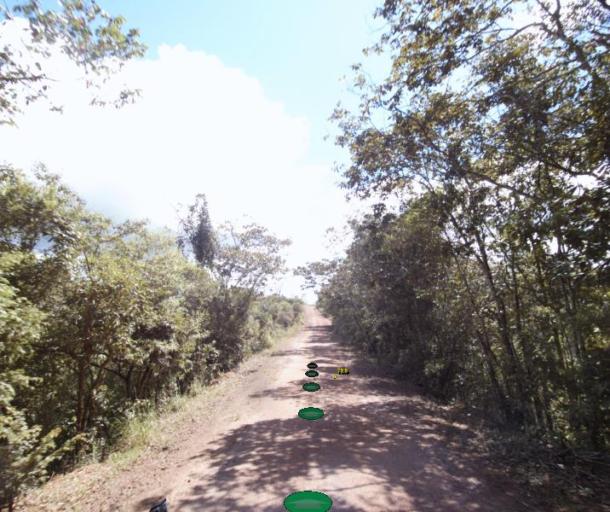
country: BR
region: Goias
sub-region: Pirenopolis
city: Pirenopolis
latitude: -15.7801
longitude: -48.8540
